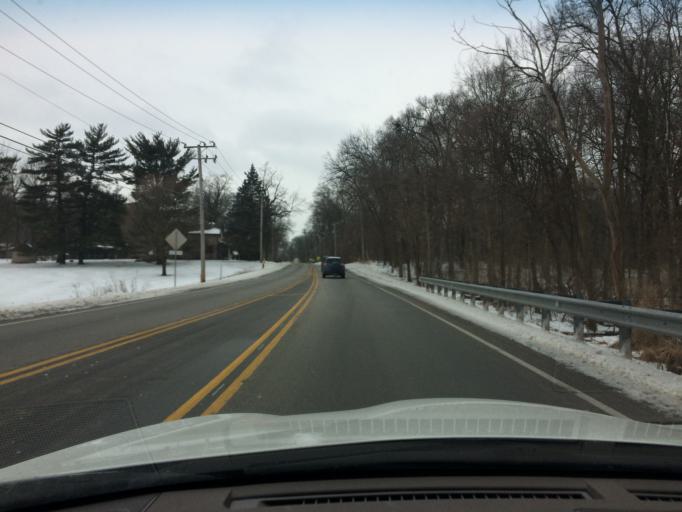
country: US
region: Illinois
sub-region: Kane County
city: Sugar Grove
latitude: 41.7865
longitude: -88.4351
